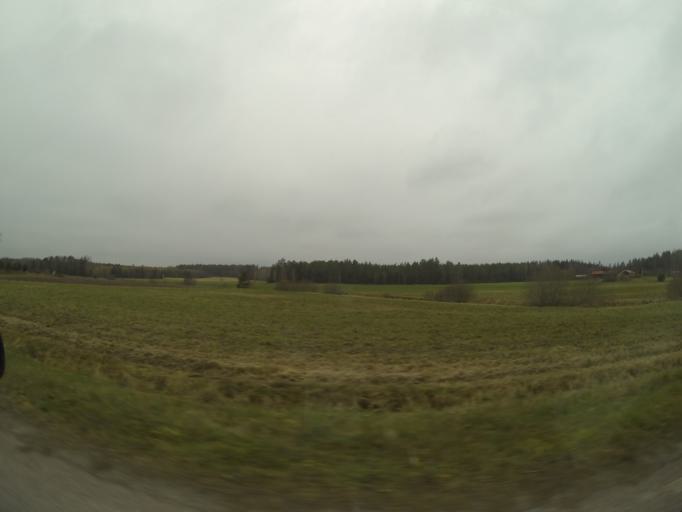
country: SE
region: Vaestmanland
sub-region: Kopings Kommun
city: Koping
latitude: 59.5864
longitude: 16.0862
